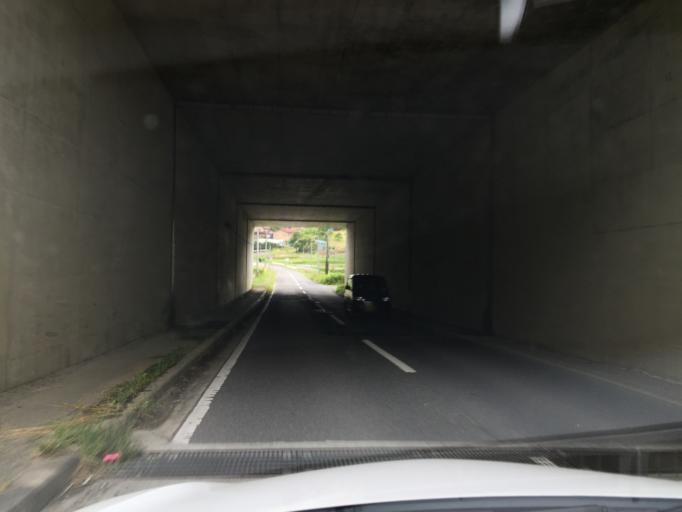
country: JP
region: Fukushima
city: Funehikimachi-funehiki
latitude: 37.4265
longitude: 140.5510
